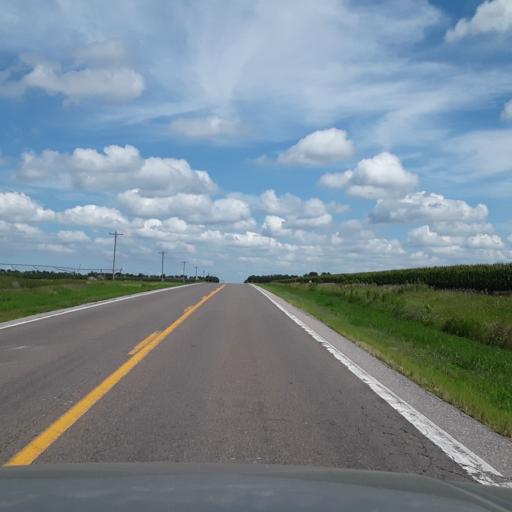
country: US
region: Nebraska
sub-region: Polk County
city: Osceola
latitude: 41.0944
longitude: -97.4259
